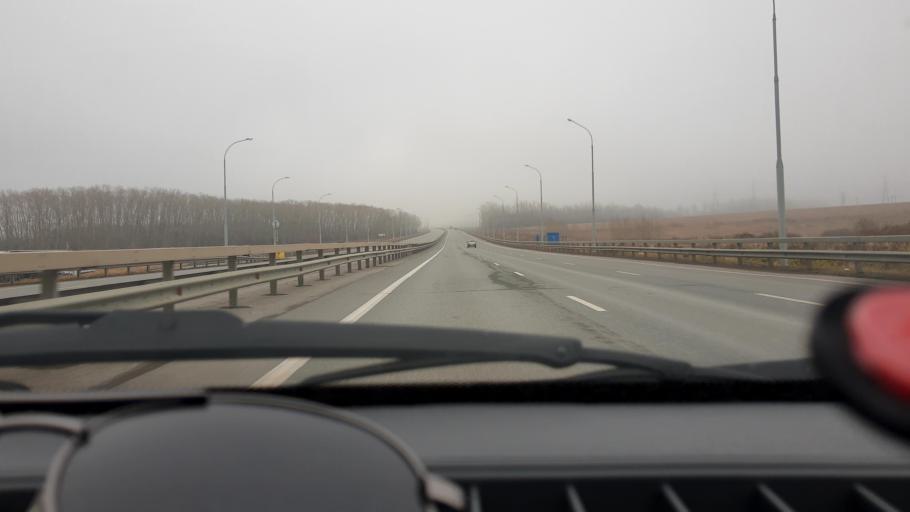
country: RU
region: Bashkortostan
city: Kabakovo
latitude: 54.6518
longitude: 56.0920
